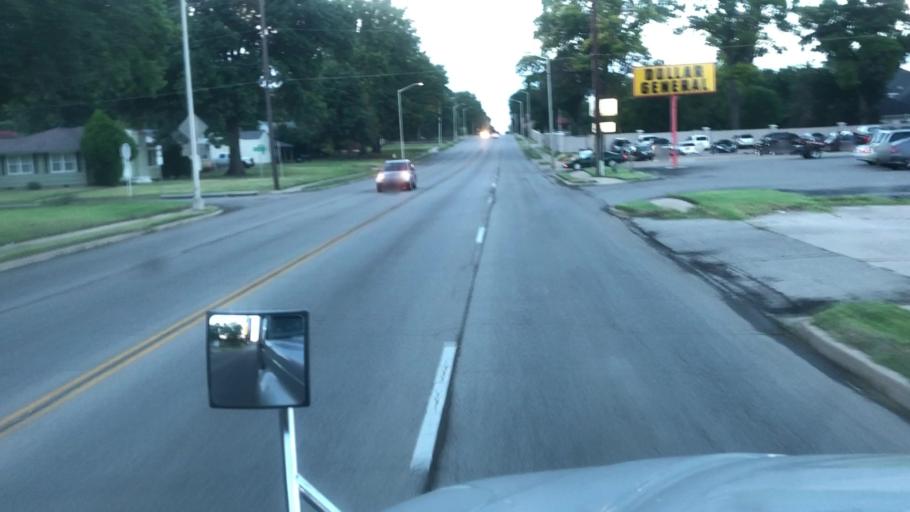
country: US
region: Oklahoma
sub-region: Kay County
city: Ponca City
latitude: 36.7114
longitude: -97.0673
